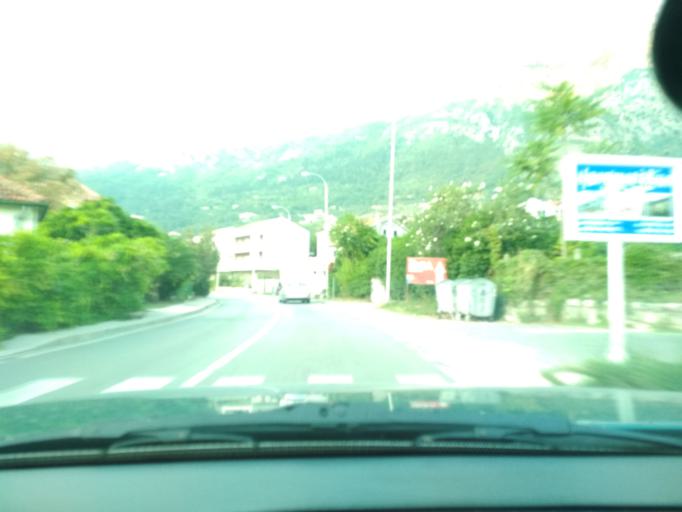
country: ME
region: Kotor
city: Risan
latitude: 42.5088
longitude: 18.6964
